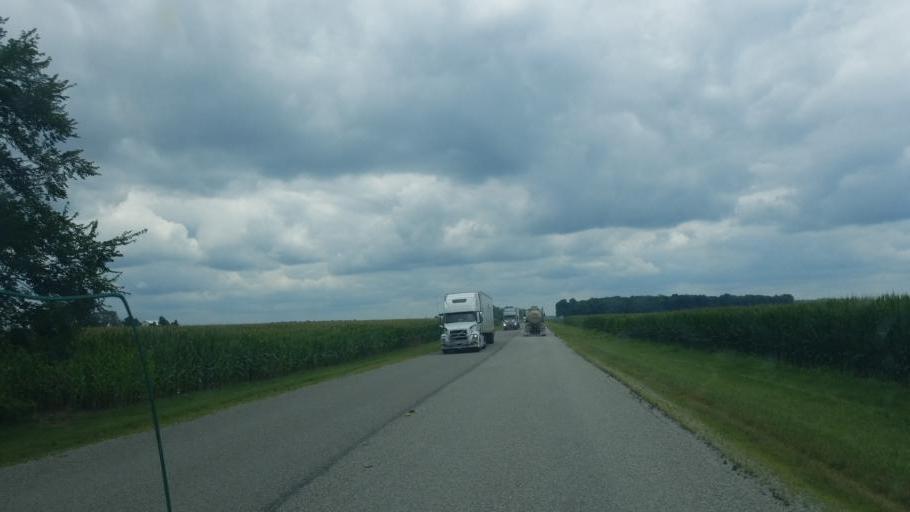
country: US
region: Indiana
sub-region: Wells County
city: Bluffton
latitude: 40.6553
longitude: -85.1295
